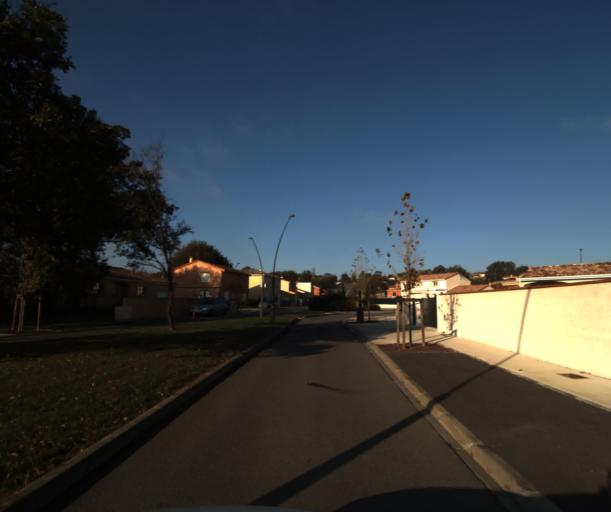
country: FR
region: Midi-Pyrenees
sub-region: Departement de la Haute-Garonne
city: Colomiers
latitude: 43.5935
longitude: 1.3428
